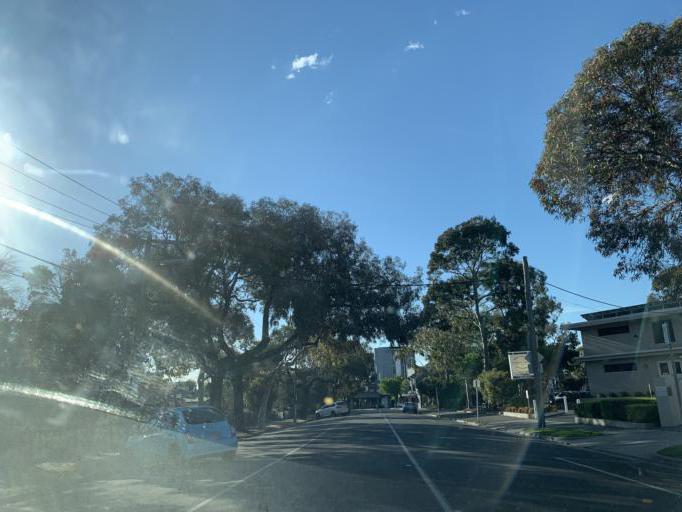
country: AU
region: Victoria
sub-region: Bayside
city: Hampton
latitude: -37.9396
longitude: 145.0035
